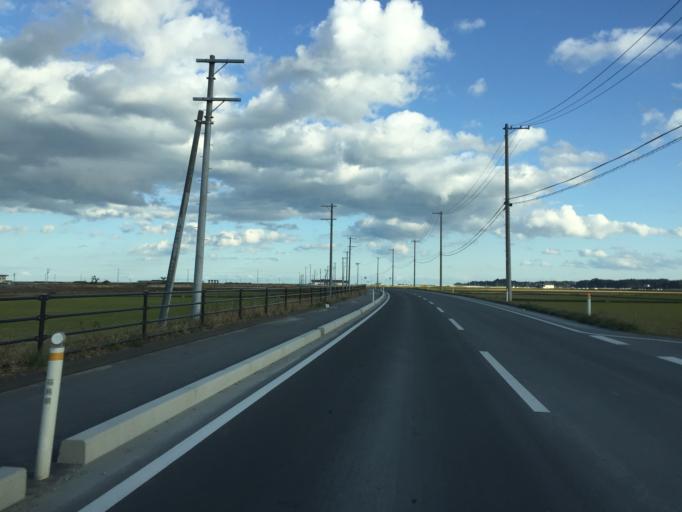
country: JP
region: Miyagi
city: Marumori
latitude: 37.7818
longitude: 140.9680
